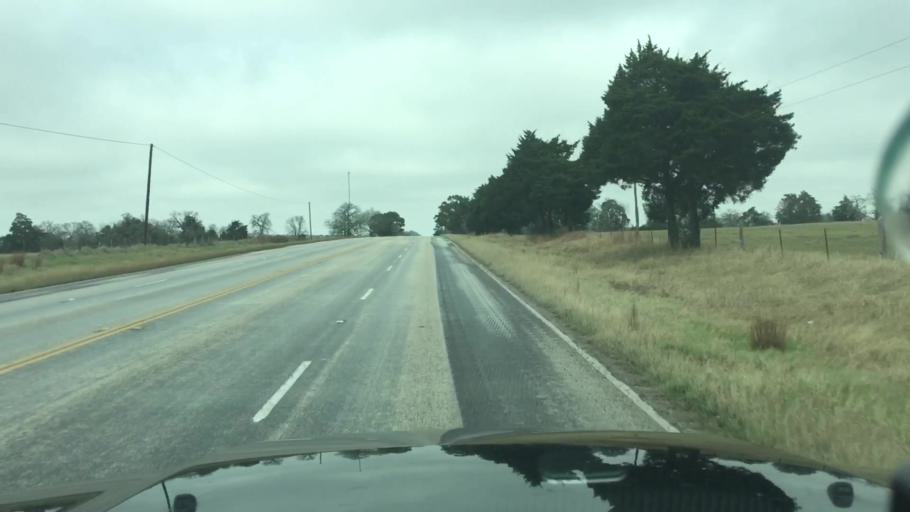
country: US
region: Texas
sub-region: Lee County
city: Giddings
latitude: 30.0985
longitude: -96.9132
